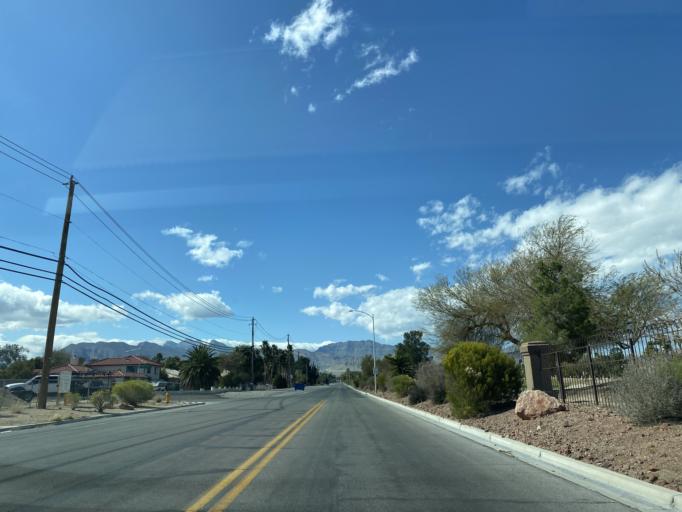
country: US
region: Nevada
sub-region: Clark County
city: Spring Valley
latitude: 36.2555
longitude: -115.2643
